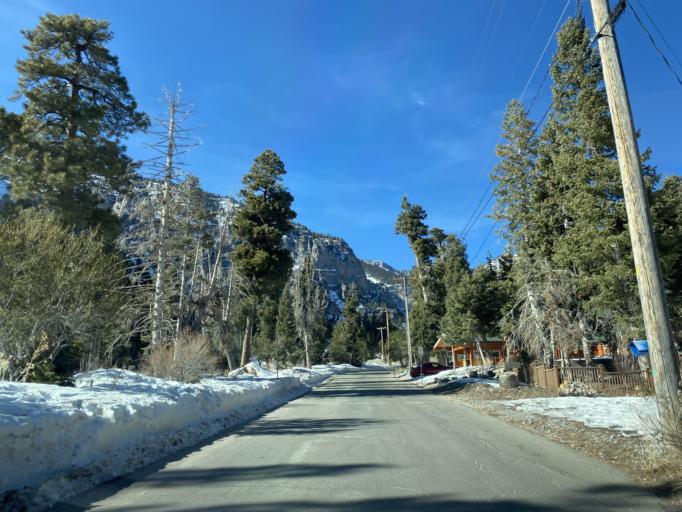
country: US
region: Nevada
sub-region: Nye County
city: Pahrump
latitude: 36.2634
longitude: -115.6554
